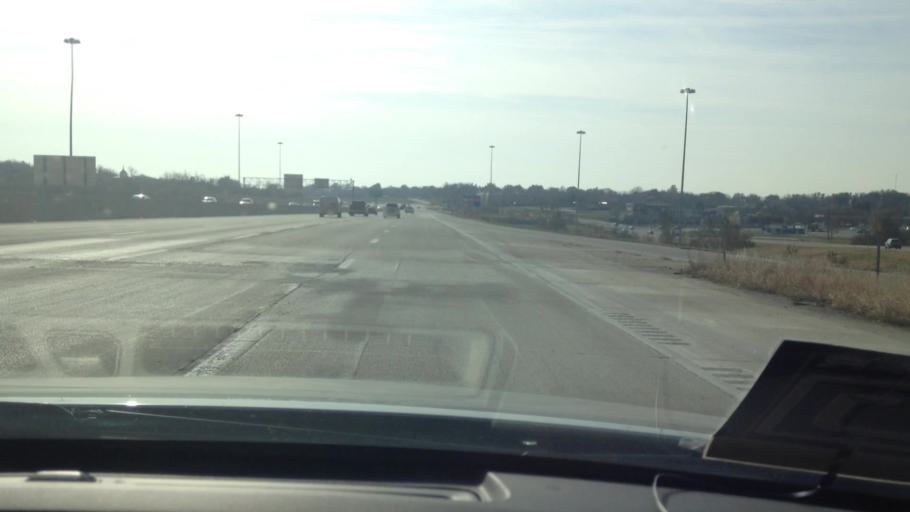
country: US
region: Missouri
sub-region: Jackson County
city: Grandview
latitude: 38.9280
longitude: -94.5277
